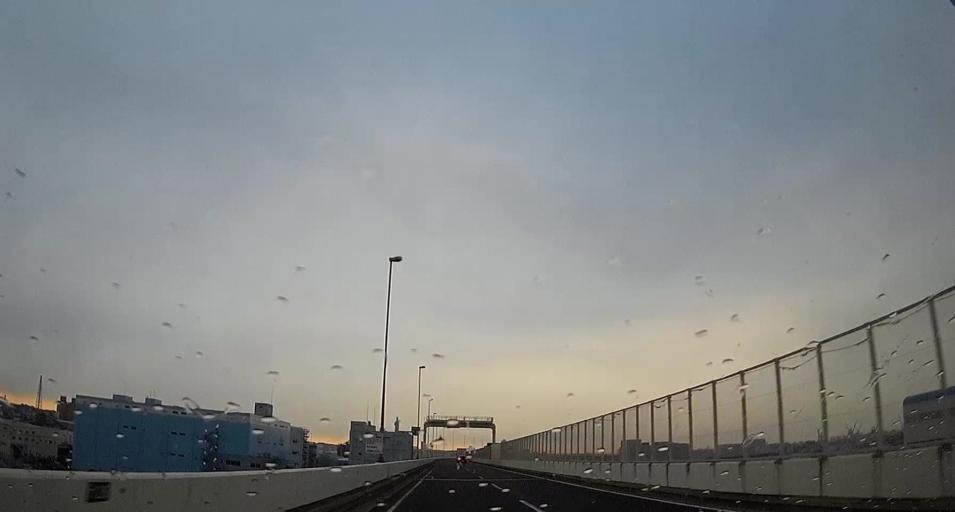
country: JP
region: Kanagawa
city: Yokohama
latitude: 35.4759
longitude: 139.6752
